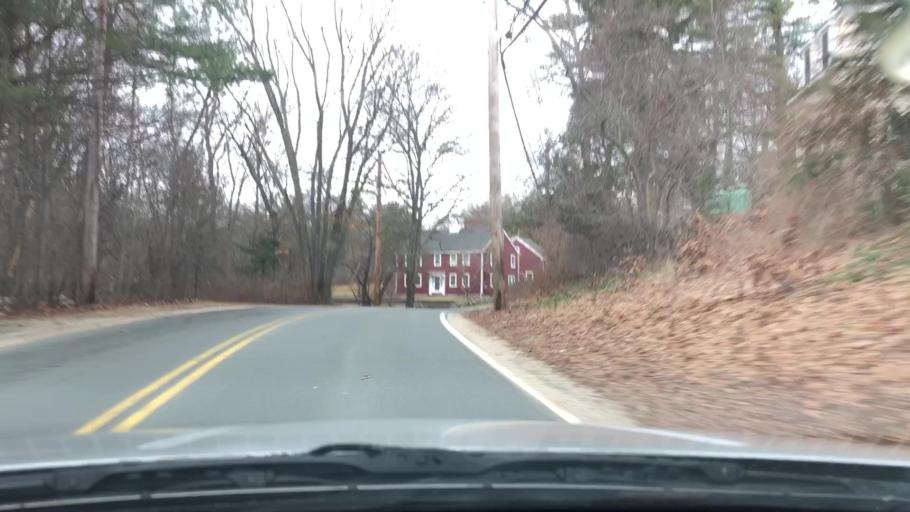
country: US
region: Massachusetts
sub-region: Essex County
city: Boxford
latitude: 42.6790
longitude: -70.9845
